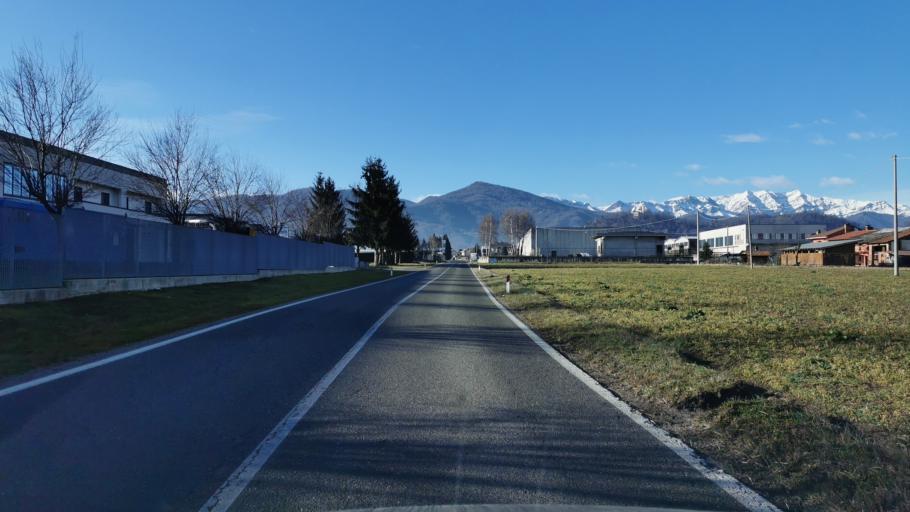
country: IT
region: Piedmont
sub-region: Provincia di Cuneo
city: Caraglio
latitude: 44.4268
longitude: 7.4444
